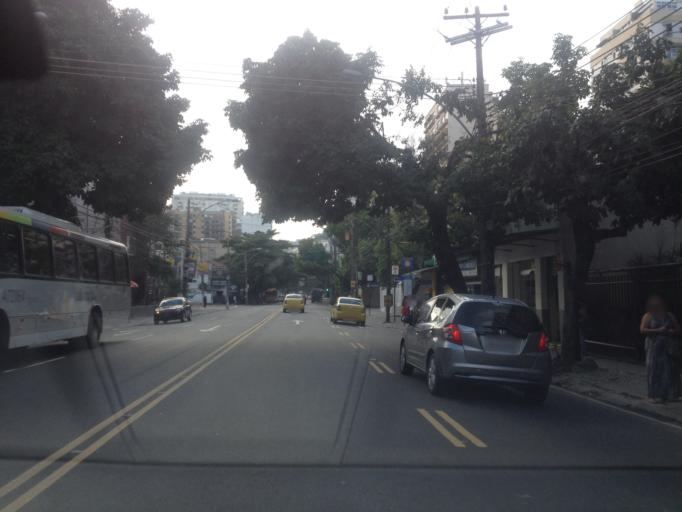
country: BR
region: Rio de Janeiro
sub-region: Rio De Janeiro
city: Rio de Janeiro
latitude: -22.9607
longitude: -43.2071
